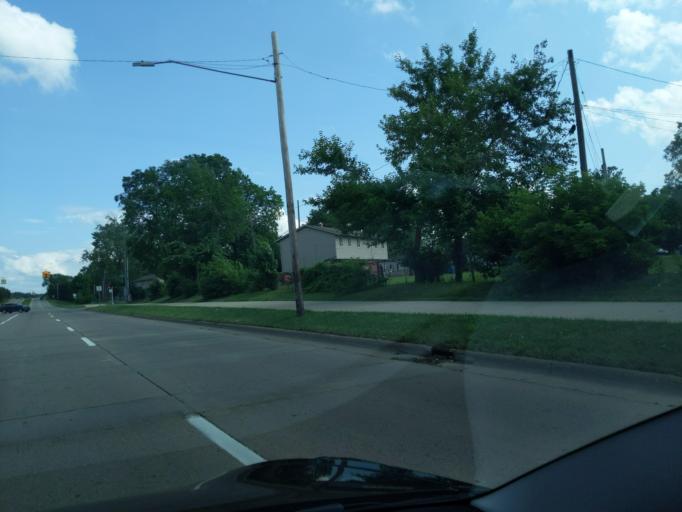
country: US
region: Michigan
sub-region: Jackson County
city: Jackson
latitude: 42.2404
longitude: -84.3989
